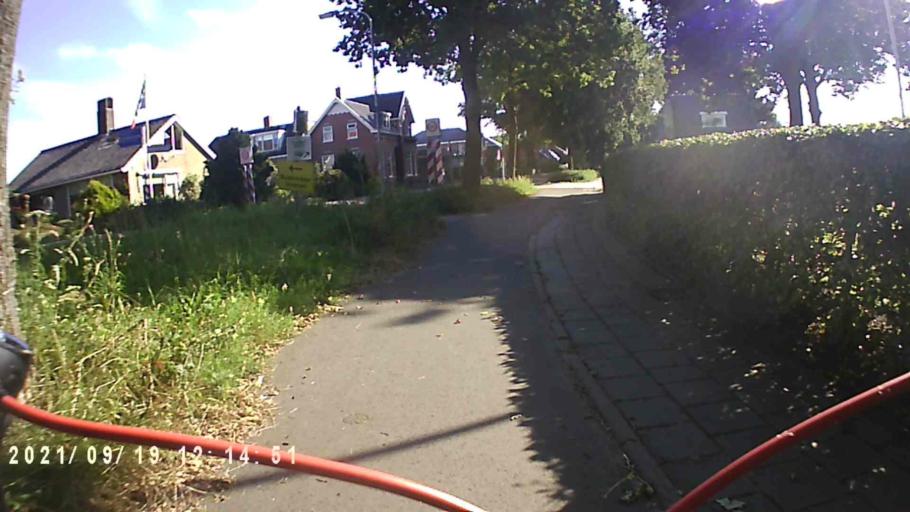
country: NL
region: Groningen
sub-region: Gemeente Slochteren
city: Slochteren
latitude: 53.2476
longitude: 6.8600
